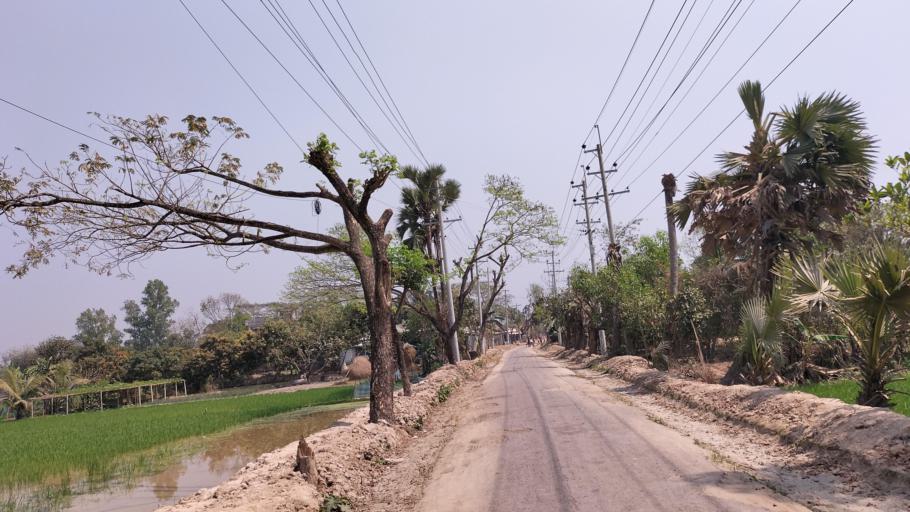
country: BD
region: Dhaka
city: Sakhipur
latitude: 24.3074
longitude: 90.3060
